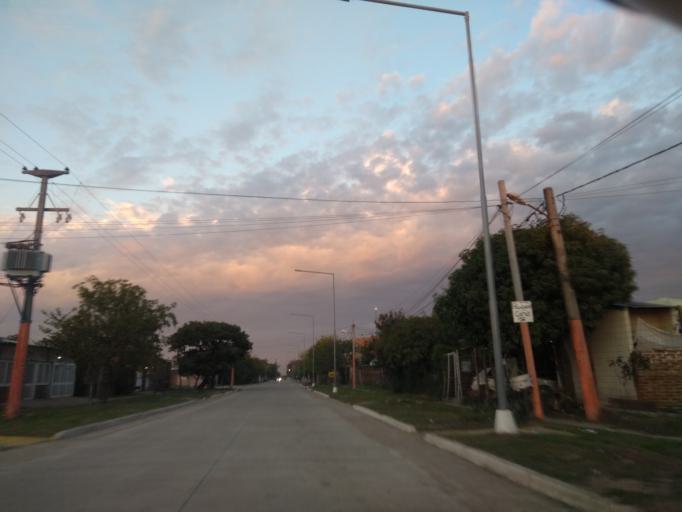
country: AR
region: Chaco
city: Resistencia
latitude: -27.4817
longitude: -58.9845
